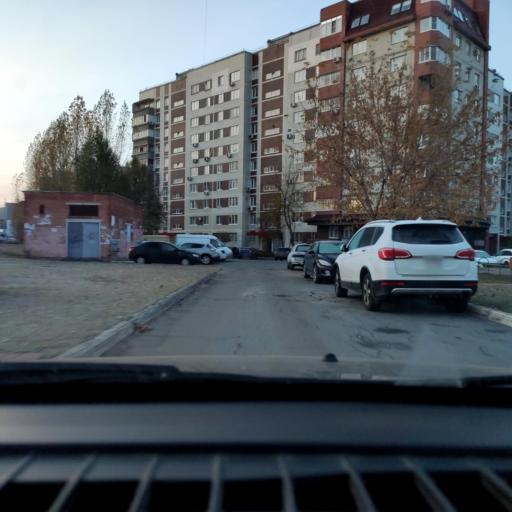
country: RU
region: Samara
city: Tol'yatti
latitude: 53.5440
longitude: 49.3627
